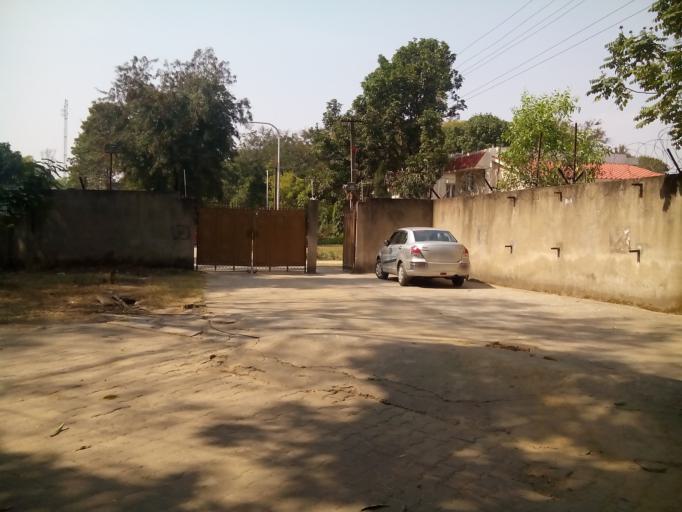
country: IN
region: Jharkhand
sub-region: Ranchi
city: Ranchi
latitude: 23.3908
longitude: 85.3788
